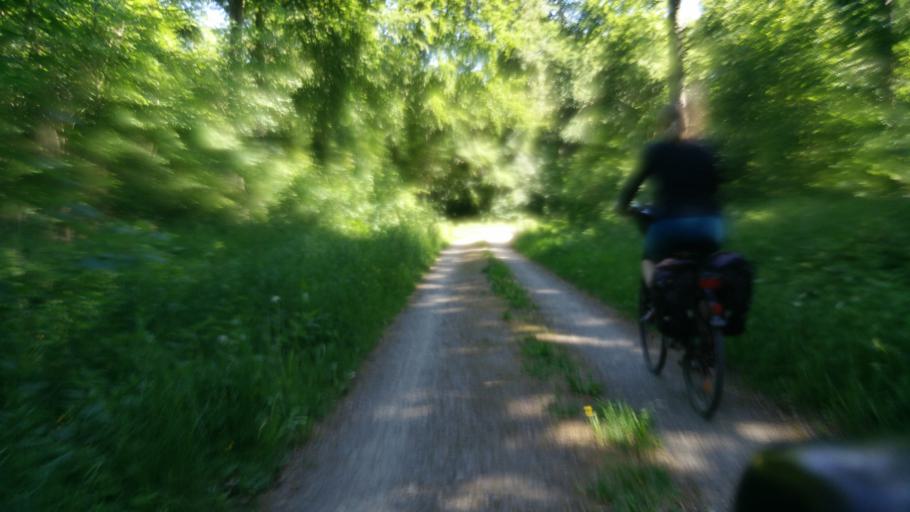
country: DE
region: Lower Saxony
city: Haste
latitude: 52.3891
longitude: 9.3924
